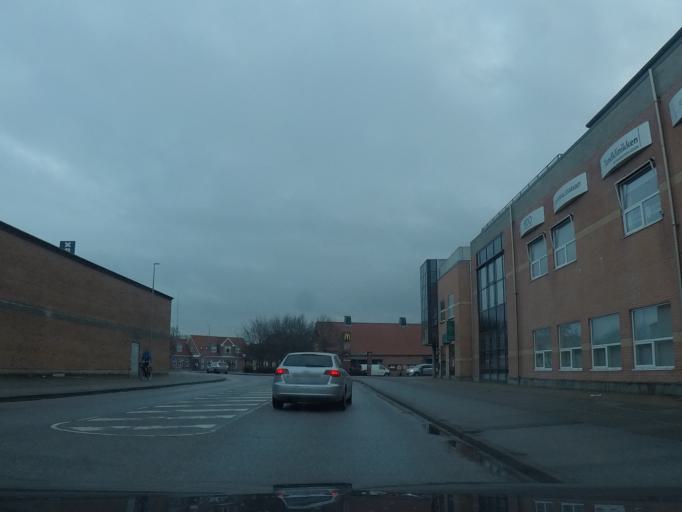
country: DK
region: South Denmark
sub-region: Varde Kommune
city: Varde
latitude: 55.6253
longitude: 8.4796
